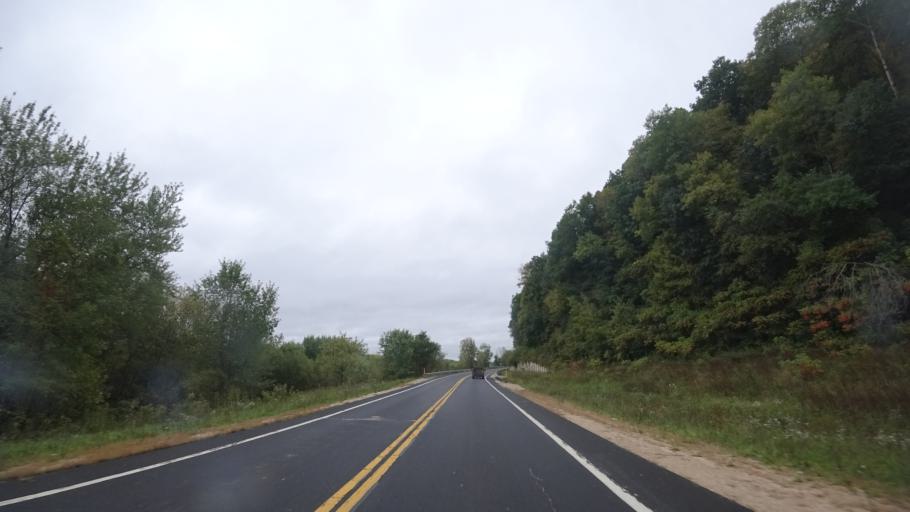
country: US
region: Wisconsin
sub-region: Grant County
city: Boscobel
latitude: 43.1505
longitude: -90.7214
